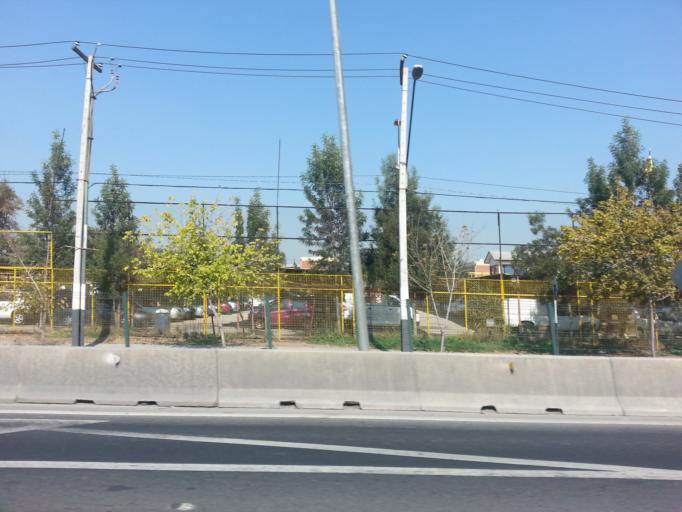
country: CL
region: Santiago Metropolitan
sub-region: Provincia de Santiago
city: La Pintana
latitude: -33.5408
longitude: -70.6469
